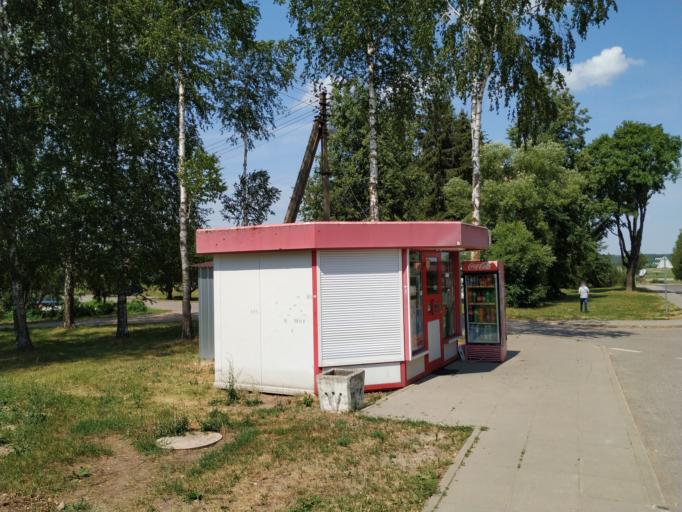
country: LT
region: Vilnius County
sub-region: Vilnius
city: Fabijoniskes
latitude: 54.8061
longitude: 25.2568
